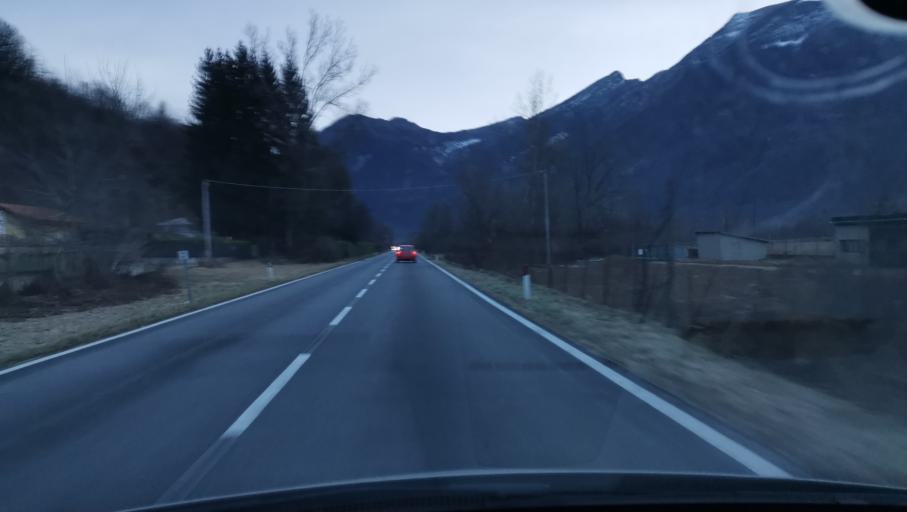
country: IT
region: Piedmont
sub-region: Provincia di Cuneo
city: Valloriate
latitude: 44.3122
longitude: 7.3498
